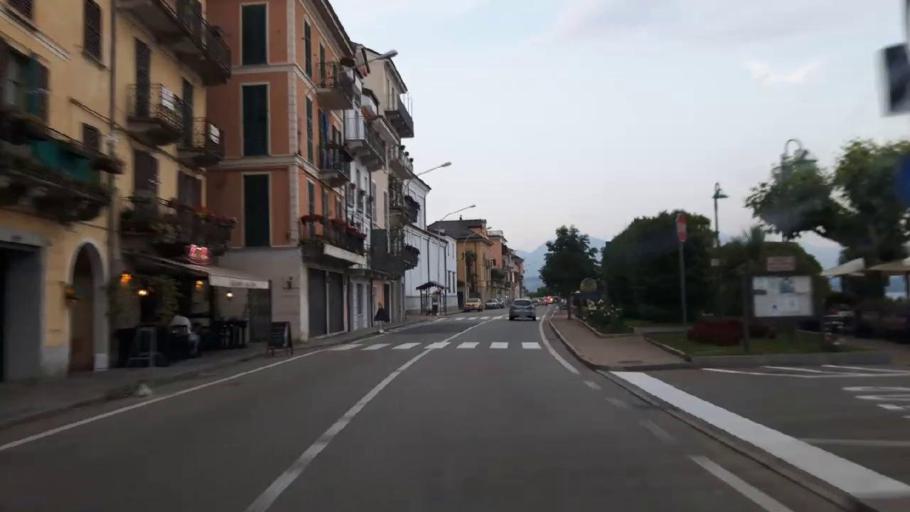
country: IT
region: Piedmont
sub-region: Provincia Verbano-Cusio-Ossola
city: Belgirate
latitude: 45.8377
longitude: 8.5717
